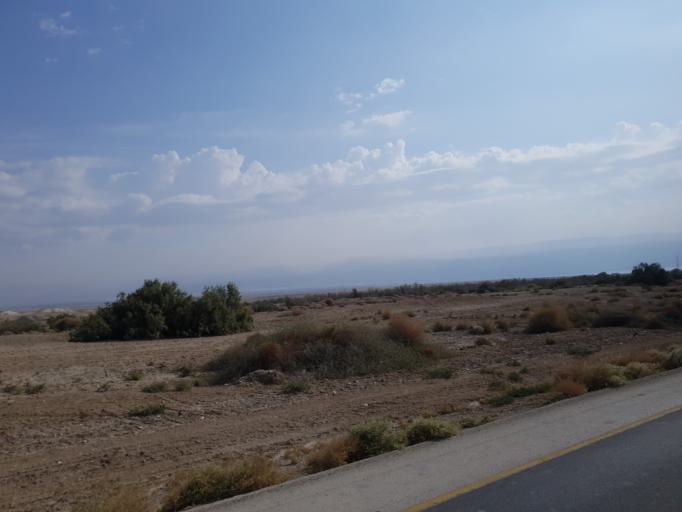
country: PS
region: West Bank
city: Jericho
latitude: 31.7858
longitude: 35.5002
